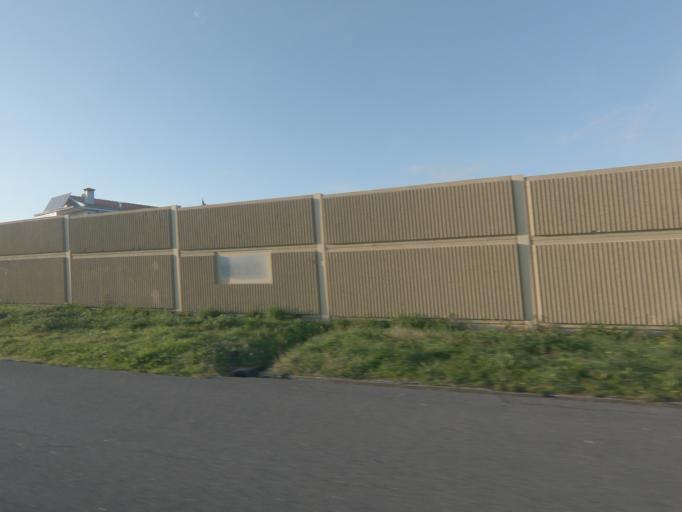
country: PT
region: Porto
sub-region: Lousada
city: Meinedo
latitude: 41.2200
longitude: -8.2414
